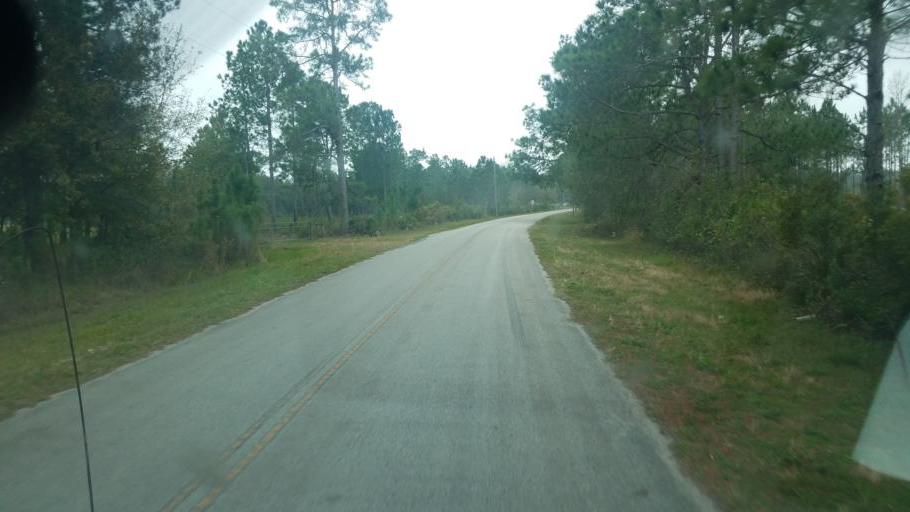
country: US
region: Florida
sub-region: Lake County
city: Groveland
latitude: 28.3855
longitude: -81.8401
